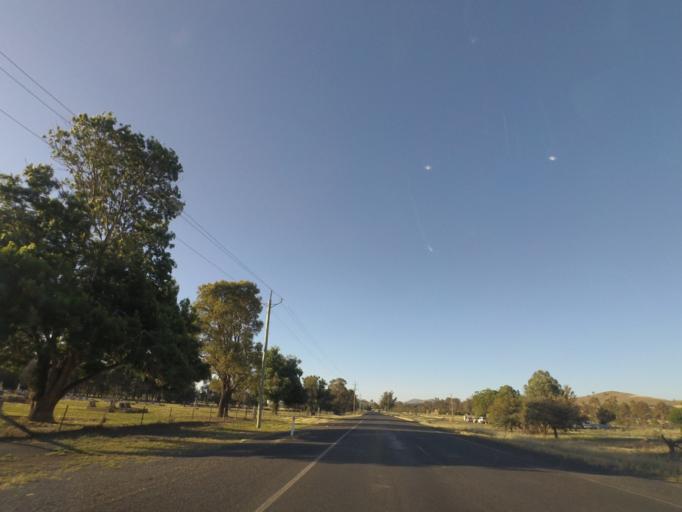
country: AU
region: New South Wales
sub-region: Gundagai
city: Gundagai
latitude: -34.9325
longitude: 148.1668
